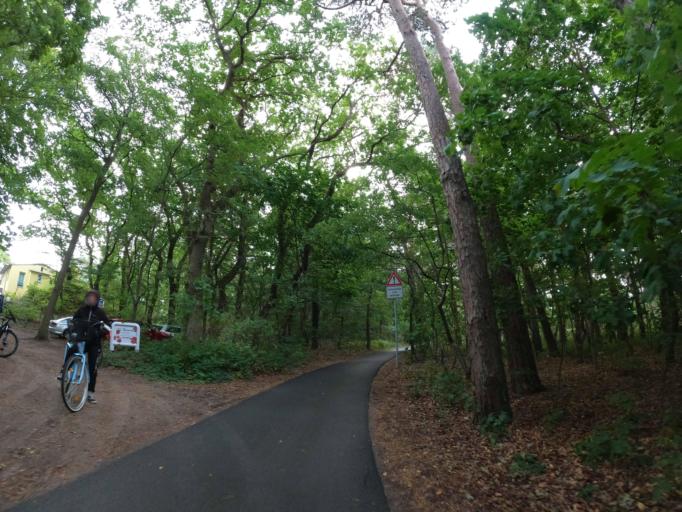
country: DE
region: Mecklenburg-Vorpommern
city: Ostseebad Gohren
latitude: 54.2790
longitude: 13.7182
